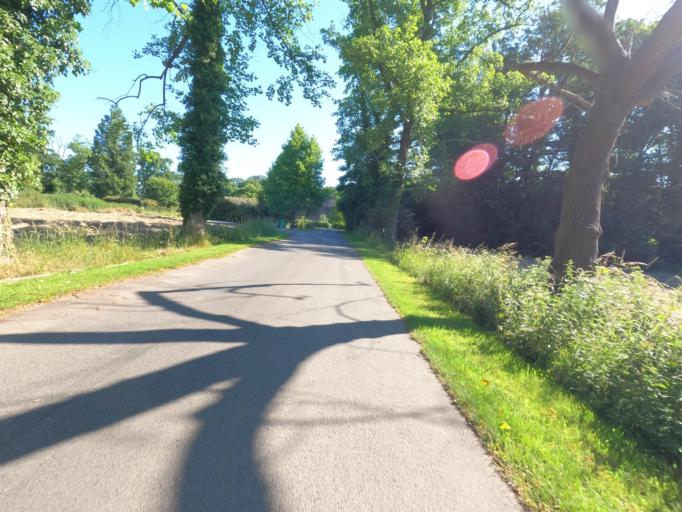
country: DE
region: North Rhine-Westphalia
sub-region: Regierungsbezirk Koln
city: Wassenberg
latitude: 51.1148
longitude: 6.1324
